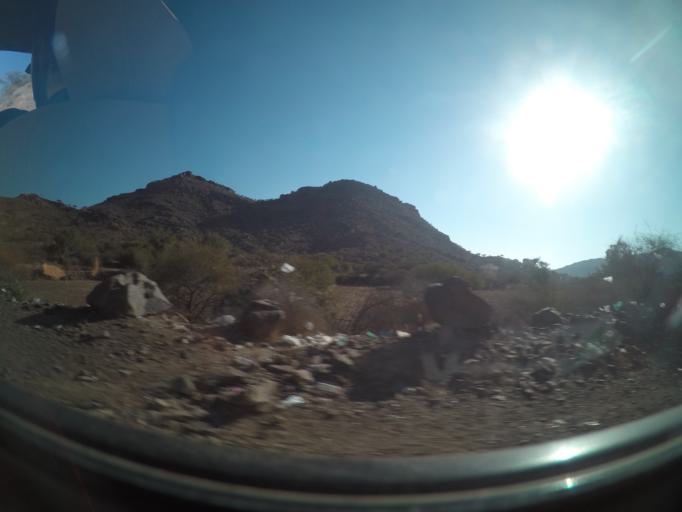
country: YE
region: Ad Dali'
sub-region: Ad Dhale'e
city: Dhalie
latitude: 13.6734
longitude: 44.7634
